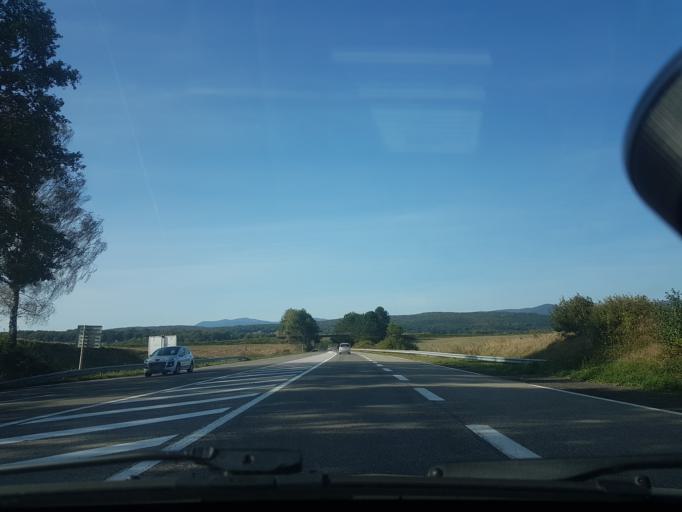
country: FR
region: Franche-Comte
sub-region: Territoire de Belfort
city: Chevremont
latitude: 47.6508
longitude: 6.9147
